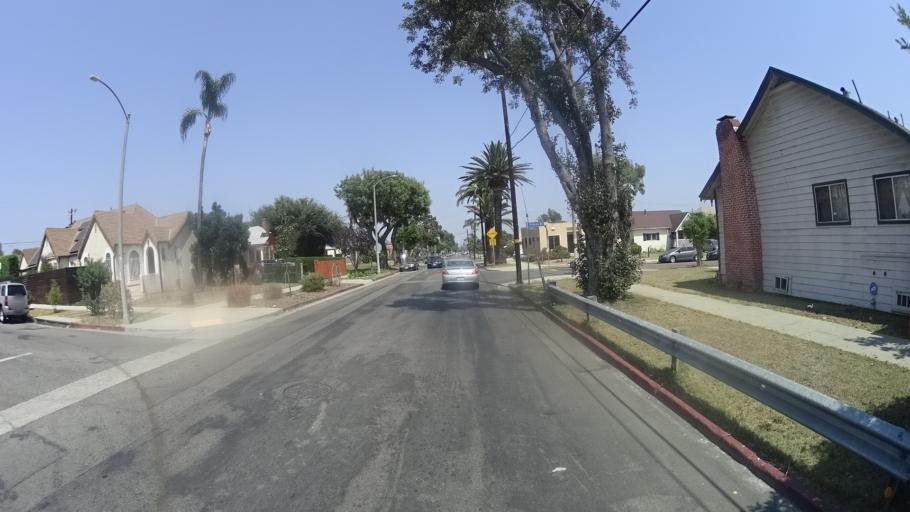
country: US
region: California
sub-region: Los Angeles County
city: View Park-Windsor Hills
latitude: 33.9853
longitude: -118.3400
